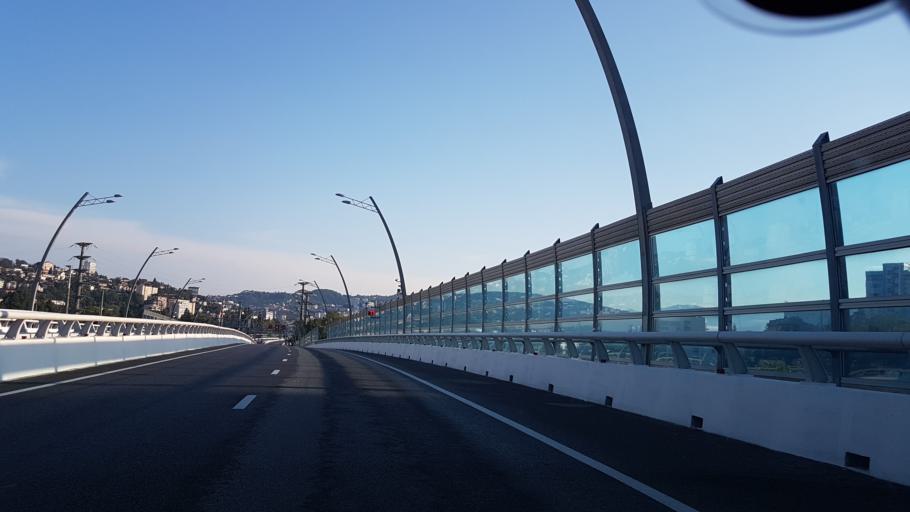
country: RU
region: Krasnodarskiy
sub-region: Sochi City
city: Sochi
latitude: 43.5963
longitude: 39.7317
